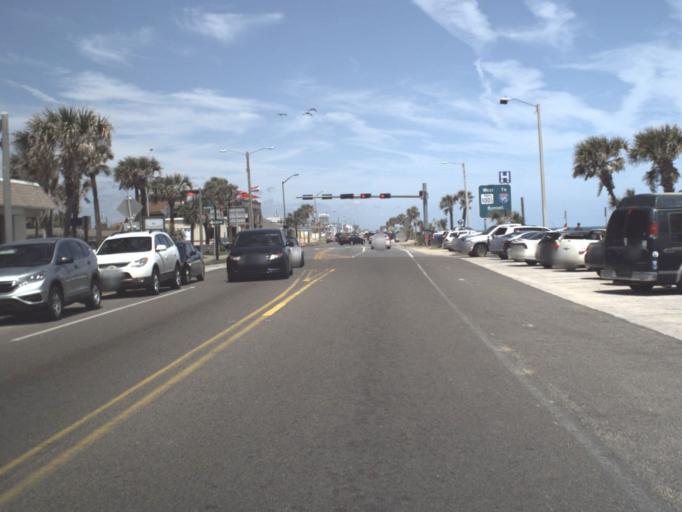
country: US
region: Florida
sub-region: Flagler County
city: Flagler Beach
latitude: 29.4800
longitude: -81.1269
